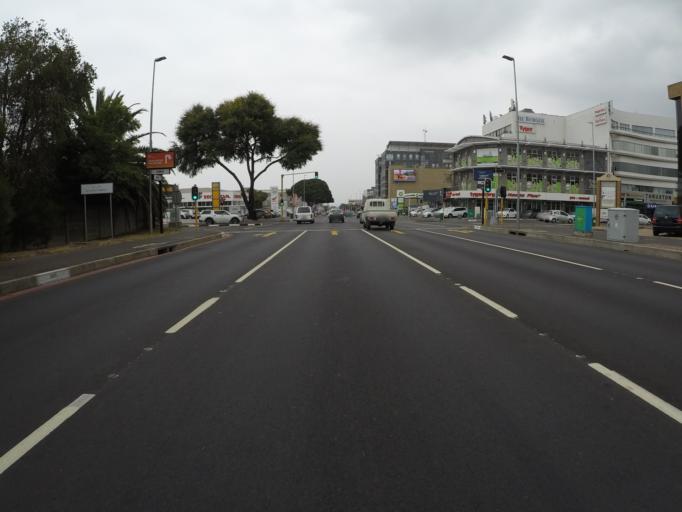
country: ZA
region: Western Cape
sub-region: City of Cape Town
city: Kraaifontein
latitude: -33.8797
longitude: 18.6367
